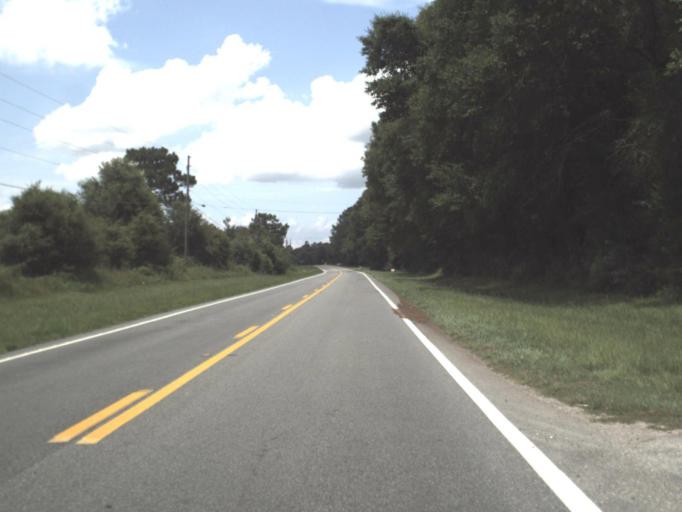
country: US
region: Florida
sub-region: Madison County
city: Madison
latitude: 30.5273
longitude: -83.3678
